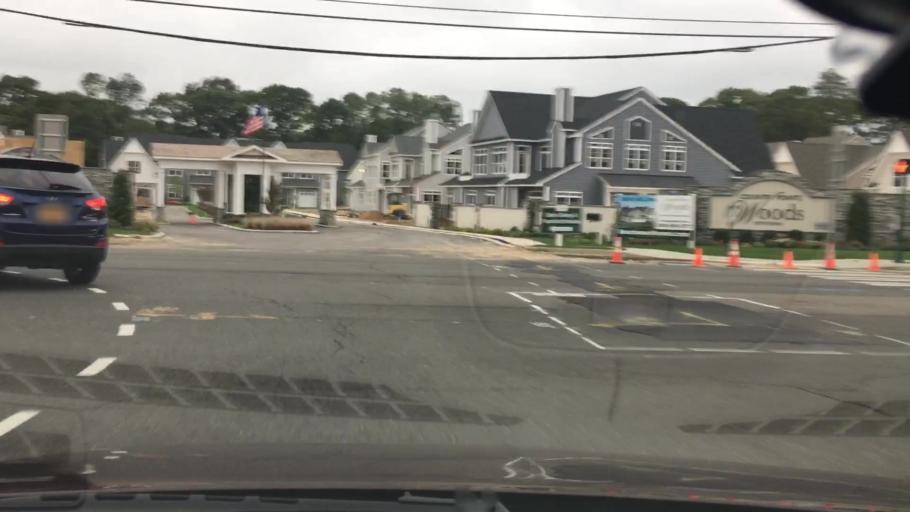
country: US
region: New York
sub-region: Suffolk County
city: Hauppauge
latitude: 40.8314
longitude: -73.1973
